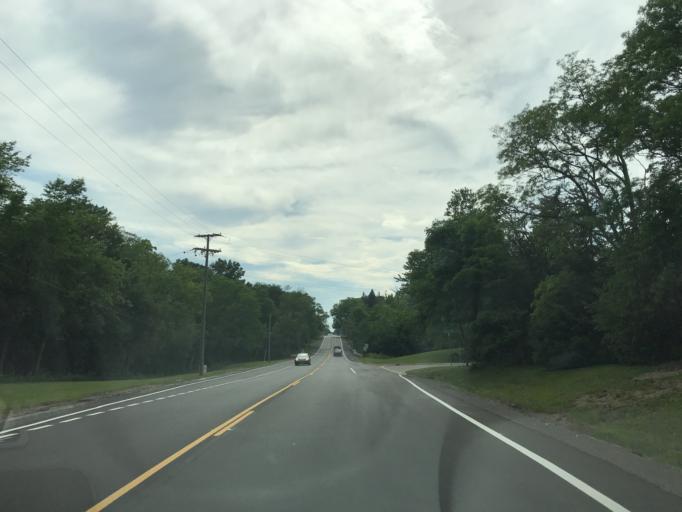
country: US
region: Michigan
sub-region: Oakland County
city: Farmington
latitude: 42.4709
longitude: -83.3290
